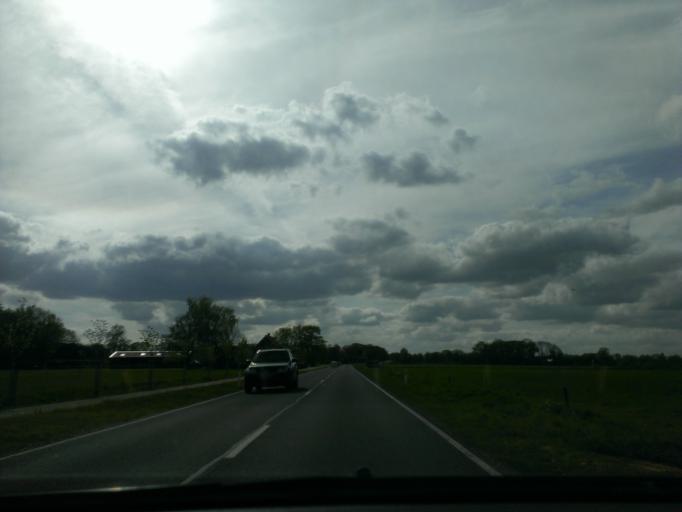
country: NL
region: Overijssel
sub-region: Gemeente Almelo
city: Almelo
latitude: 52.3086
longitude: 6.6471
